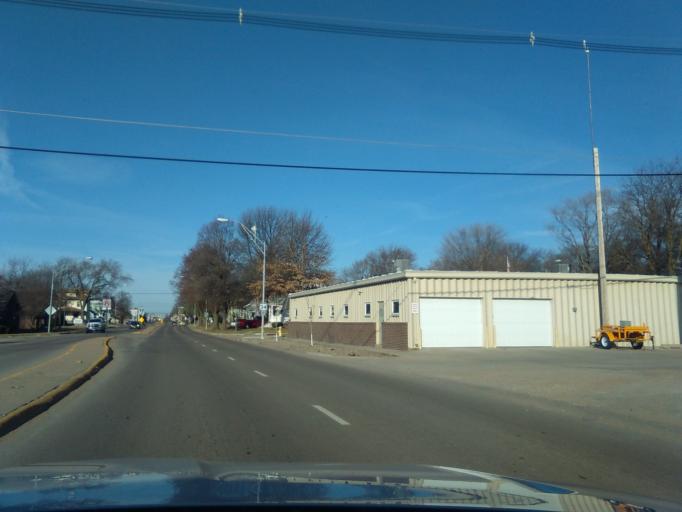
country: US
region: Nebraska
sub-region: Seward County
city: Seward
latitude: 40.9069
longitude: -97.0923
